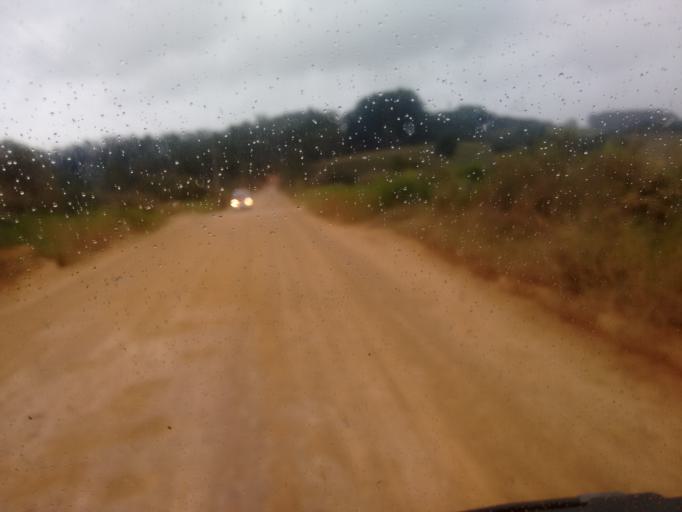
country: BR
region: Rio Grande do Sul
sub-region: Camaqua
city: Camaqua
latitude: -30.8110
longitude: -51.8228
